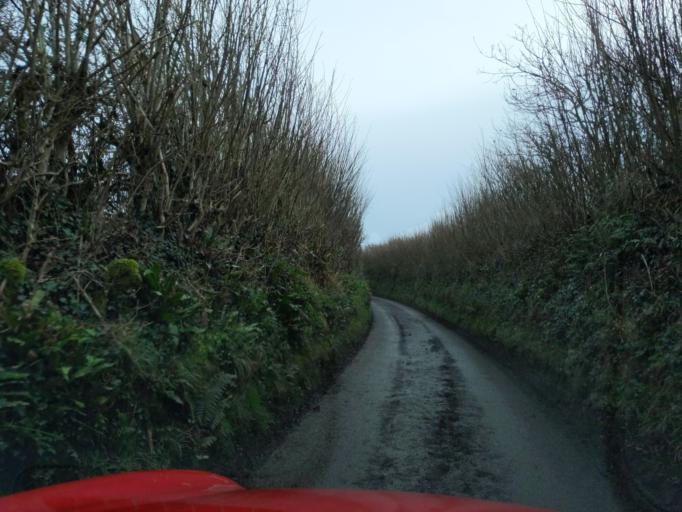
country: GB
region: England
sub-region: Cornwall
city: Duloe
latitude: 50.3539
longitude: -4.5152
